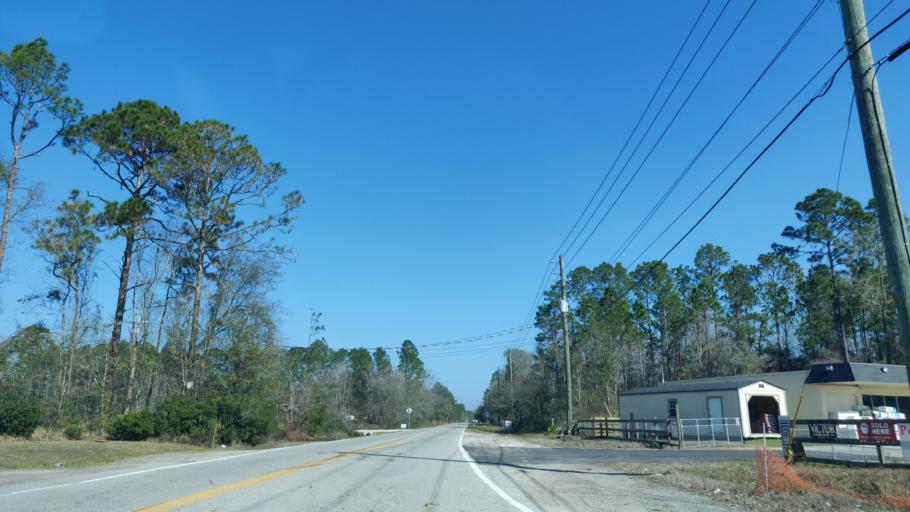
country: US
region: Florida
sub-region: Duval County
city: Baldwin
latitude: 30.2185
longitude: -81.9410
